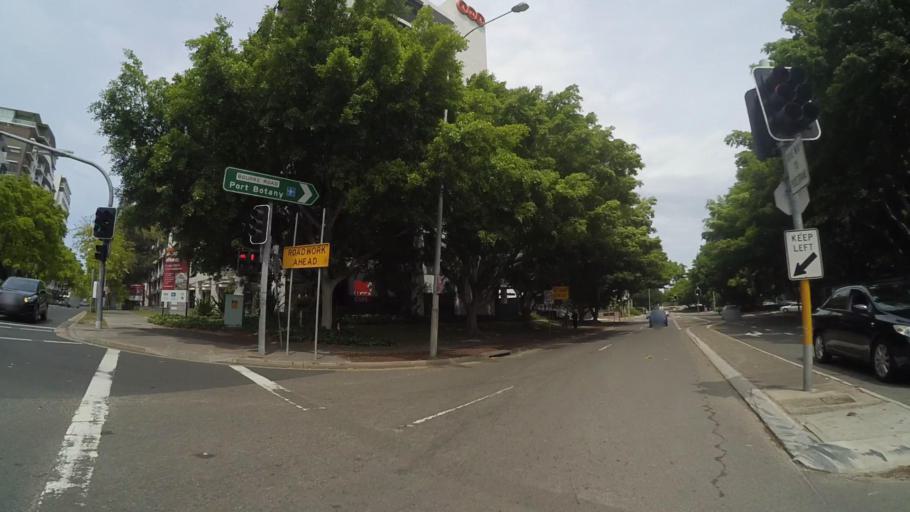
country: AU
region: New South Wales
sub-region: Botany Bay
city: Mascot
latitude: -33.9244
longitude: 151.1871
